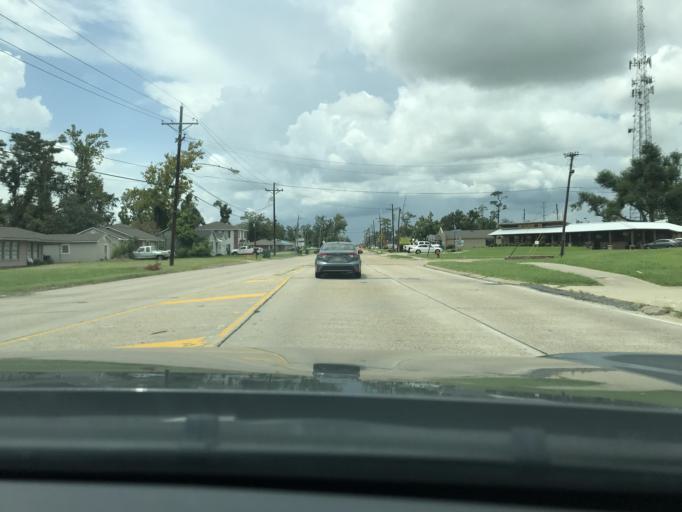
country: US
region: Louisiana
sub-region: Calcasieu Parish
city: Sulphur
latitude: 30.2274
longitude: -93.3351
